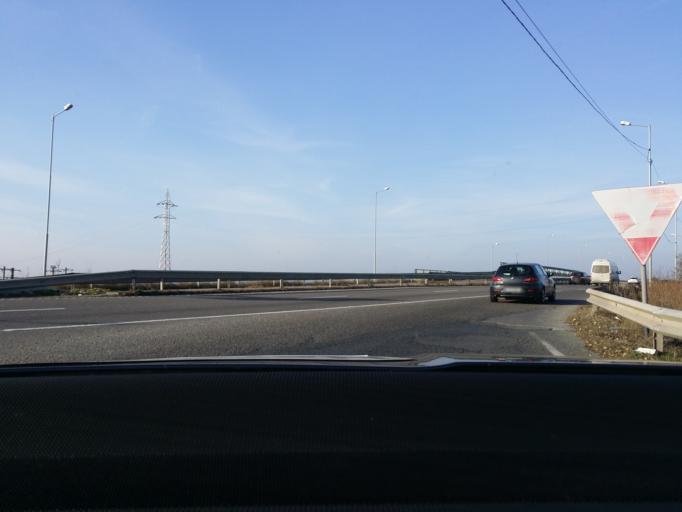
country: RO
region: Prahova
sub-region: Comuna Targsoru Vechi
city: Strejnicu
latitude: 44.9399
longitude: 25.9610
